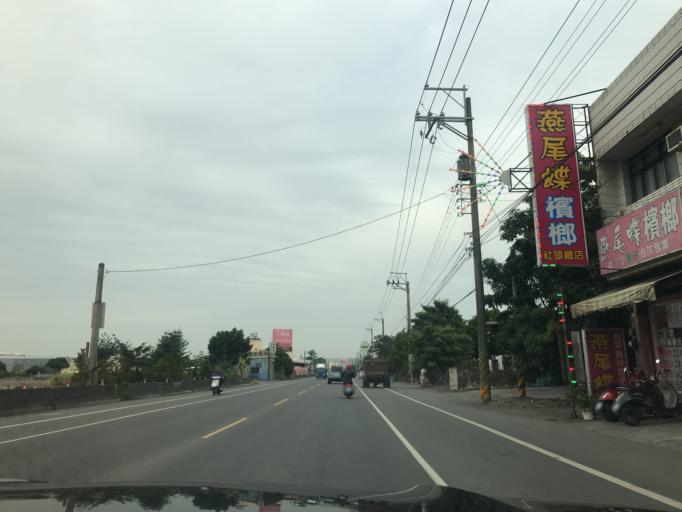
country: TW
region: Taiwan
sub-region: Nantou
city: Nantou
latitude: 23.9122
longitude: 120.5839
